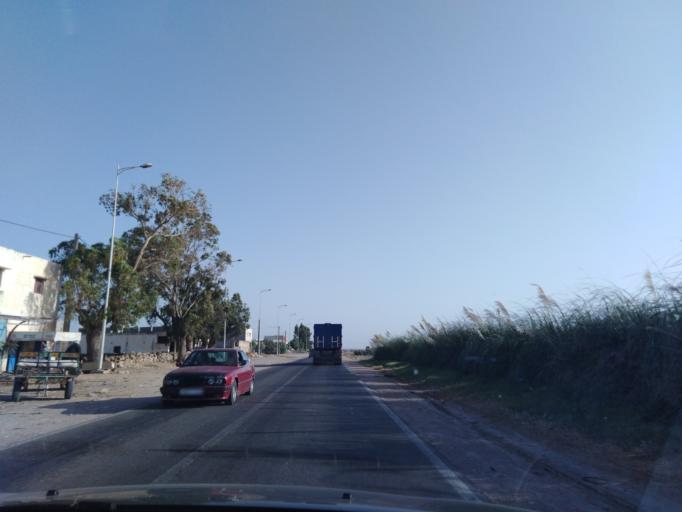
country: MA
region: Doukkala-Abda
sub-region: El-Jadida
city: Sidi Bennour
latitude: 32.5457
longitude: -8.7259
